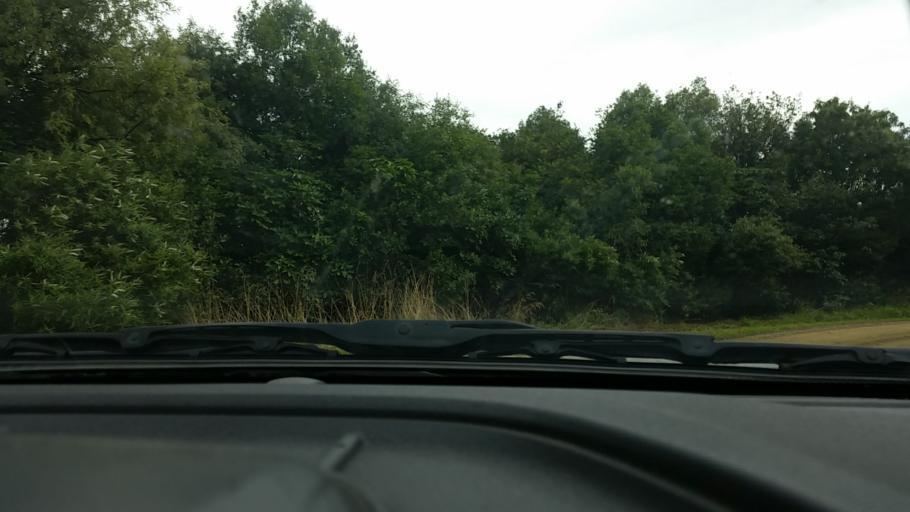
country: NZ
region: Hawke's Bay
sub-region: Wairoa District
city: Wairoa
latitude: -38.7791
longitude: 177.1290
